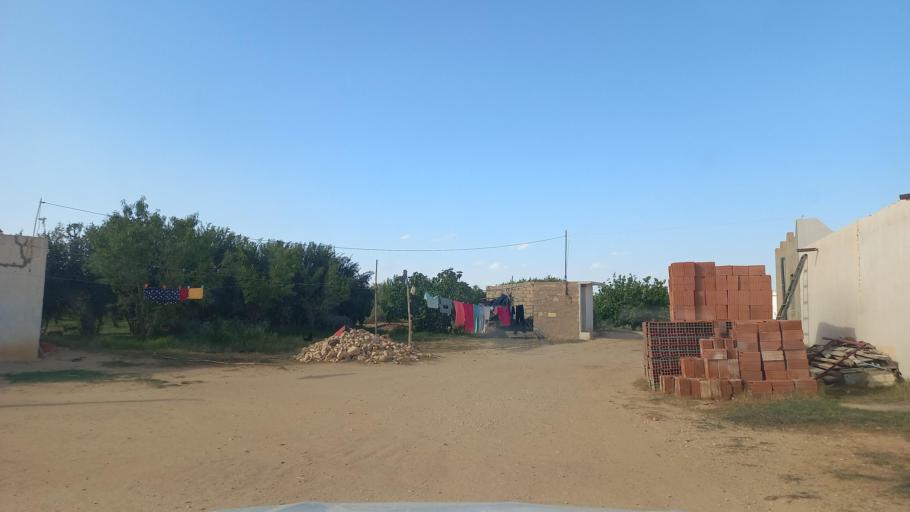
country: TN
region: Al Qasrayn
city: Kasserine
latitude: 35.2583
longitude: 9.0259
